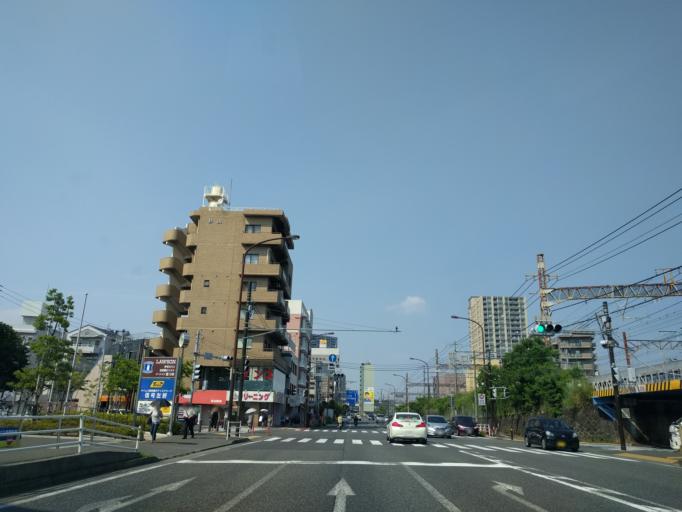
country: JP
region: Kanagawa
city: Yokohama
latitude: 35.4753
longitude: 139.6302
